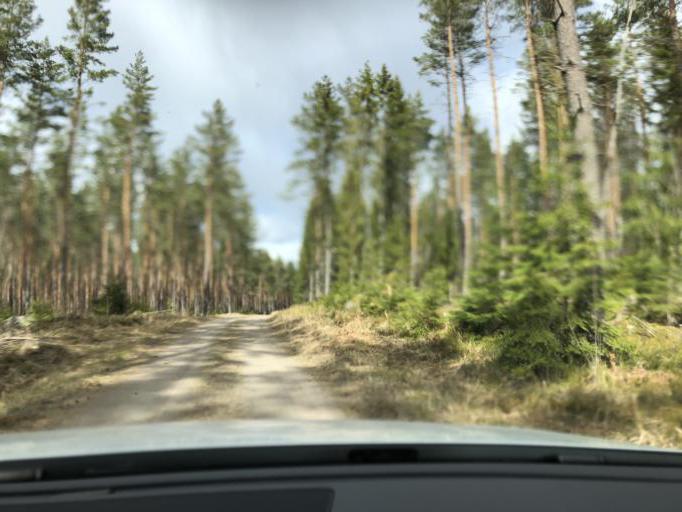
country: SE
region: Gaevleborg
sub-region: Gavle Kommun
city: Hedesunda
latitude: 60.3286
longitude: 17.1065
